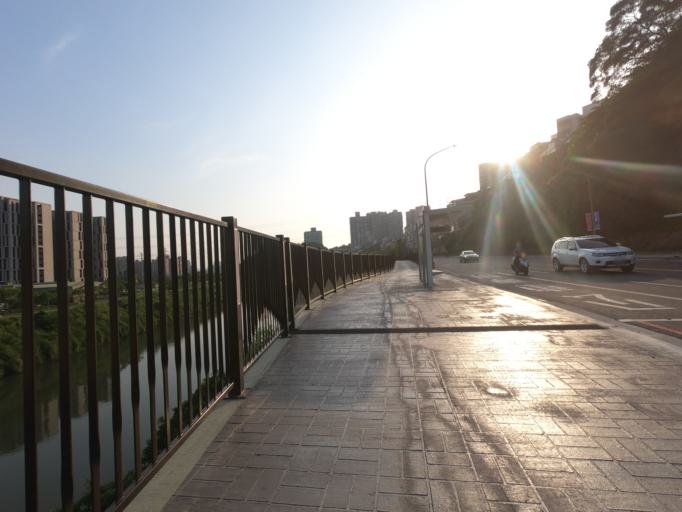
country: TW
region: Taiwan
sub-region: Keelung
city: Keelung
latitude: 25.0757
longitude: 121.6448
